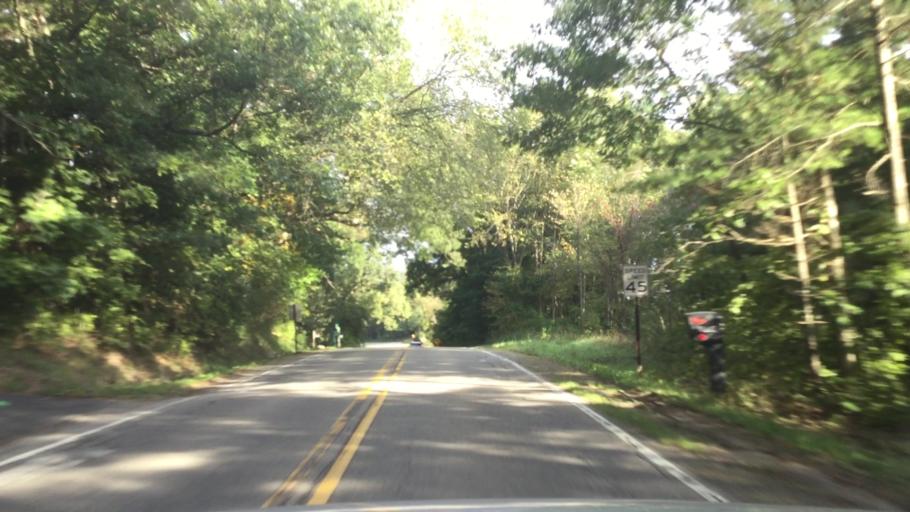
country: US
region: Michigan
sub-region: Livingston County
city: Brighton
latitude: 42.4872
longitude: -83.8521
